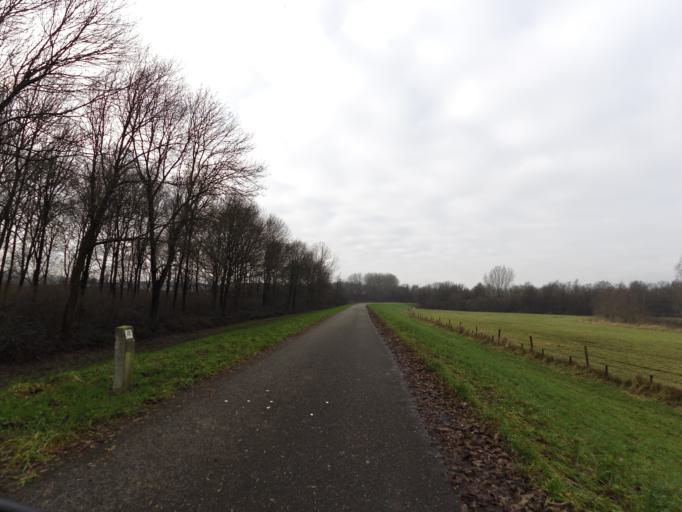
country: NL
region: Gelderland
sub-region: Gemeente Doesburg
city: Doesburg
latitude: 51.9996
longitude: 6.1502
